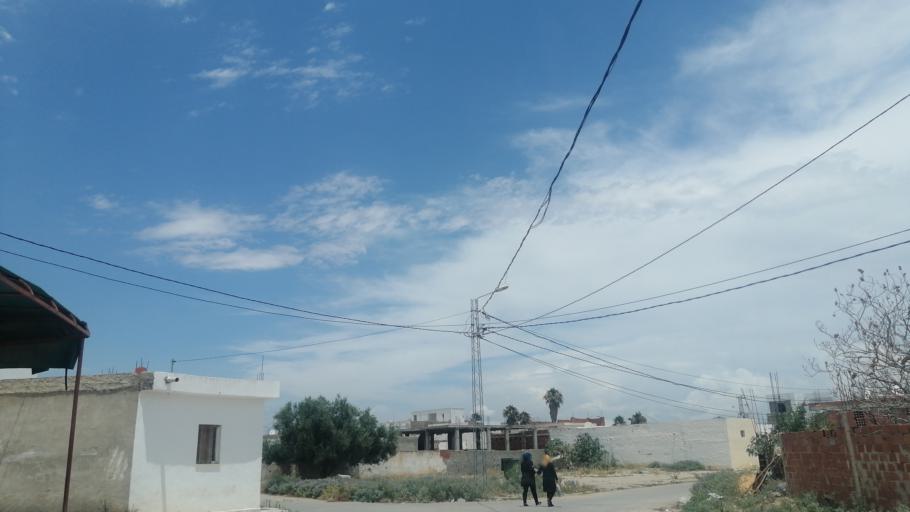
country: TN
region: Al Qayrawan
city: Sbikha
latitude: 36.1257
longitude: 10.0913
